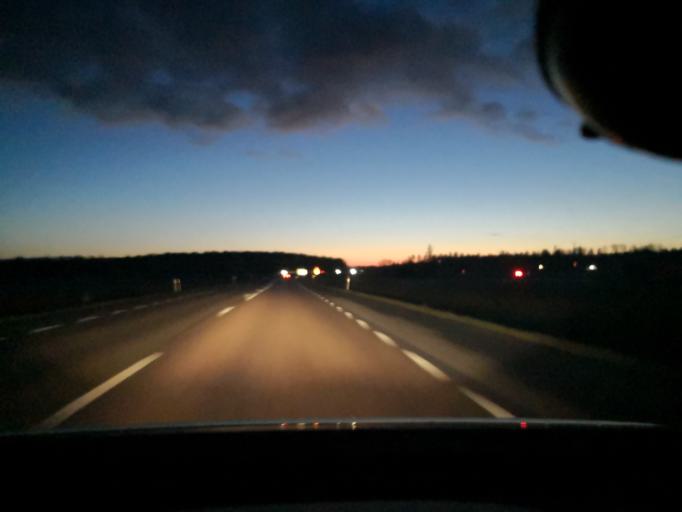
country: SE
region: Uppsala
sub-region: Heby Kommun
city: Heby
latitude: 59.9346
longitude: 16.7363
